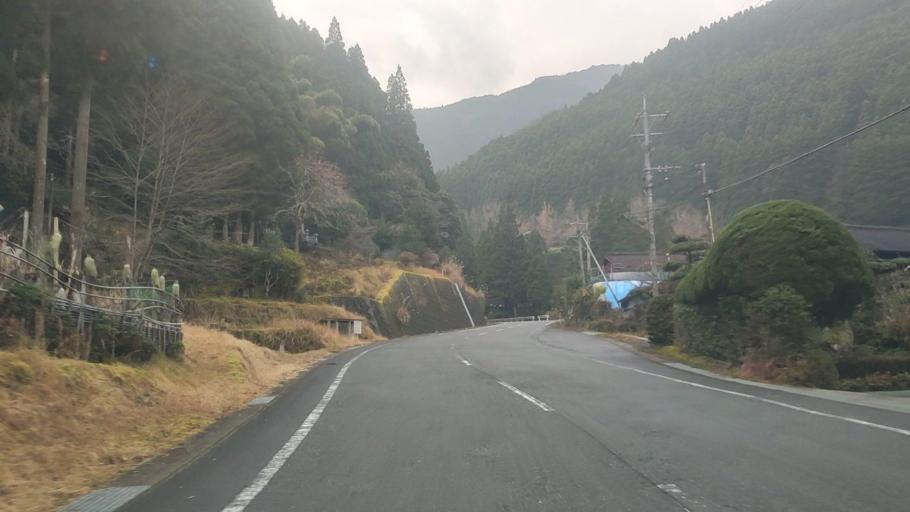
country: JP
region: Kumamoto
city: Matsubase
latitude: 32.5956
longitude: 130.8875
